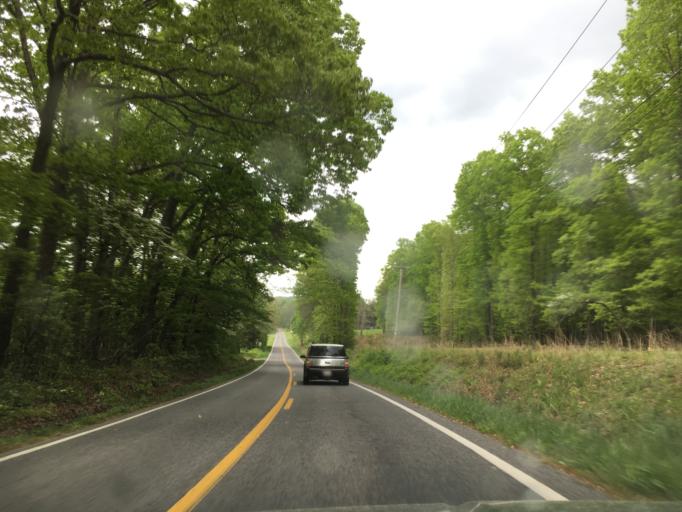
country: US
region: Virginia
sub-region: Campbell County
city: Rustburg
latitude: 37.3222
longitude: -79.1289
